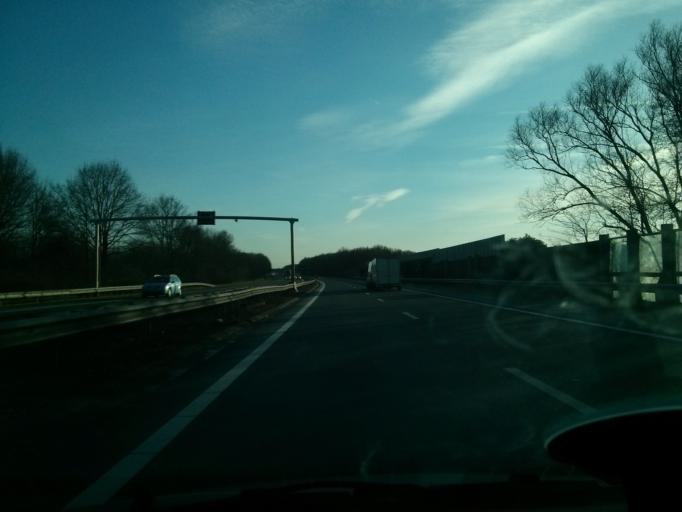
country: NL
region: Gelderland
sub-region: Gemeente Wijchen
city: Bergharen
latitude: 51.8319
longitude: 5.6846
